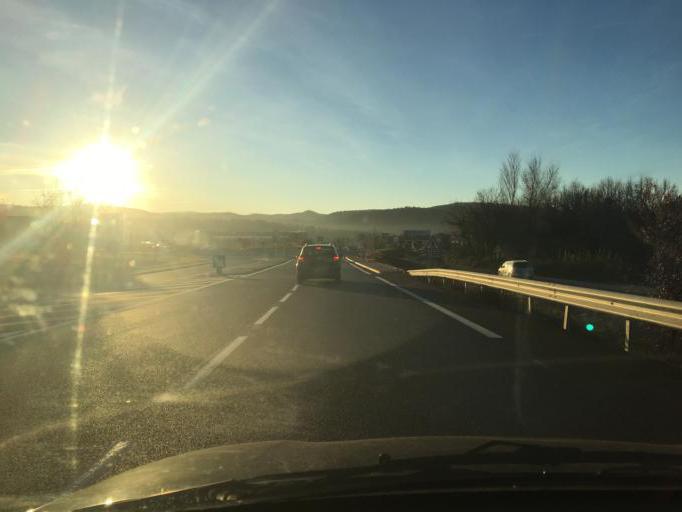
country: FR
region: Provence-Alpes-Cote d'Azur
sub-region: Departement du Var
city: Les Arcs
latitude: 43.4547
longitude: 6.4897
